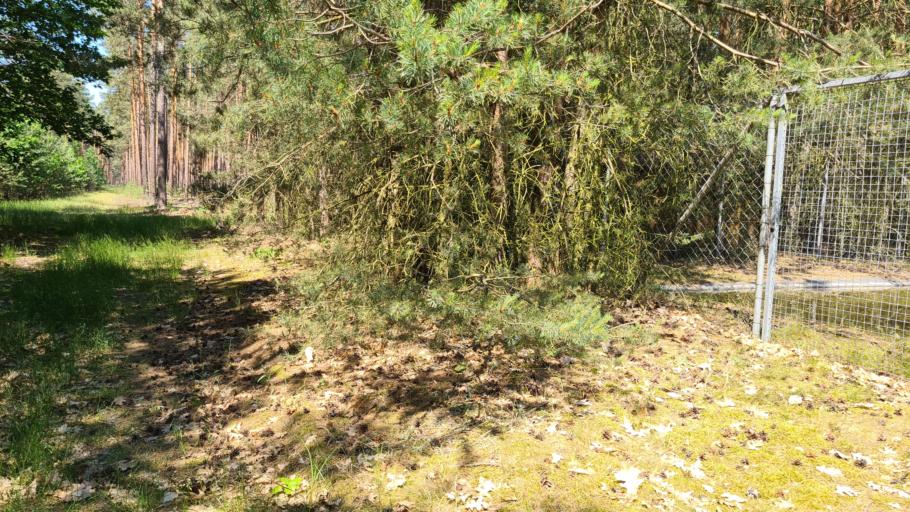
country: DE
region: Brandenburg
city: Schlieben
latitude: 51.7765
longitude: 13.3582
